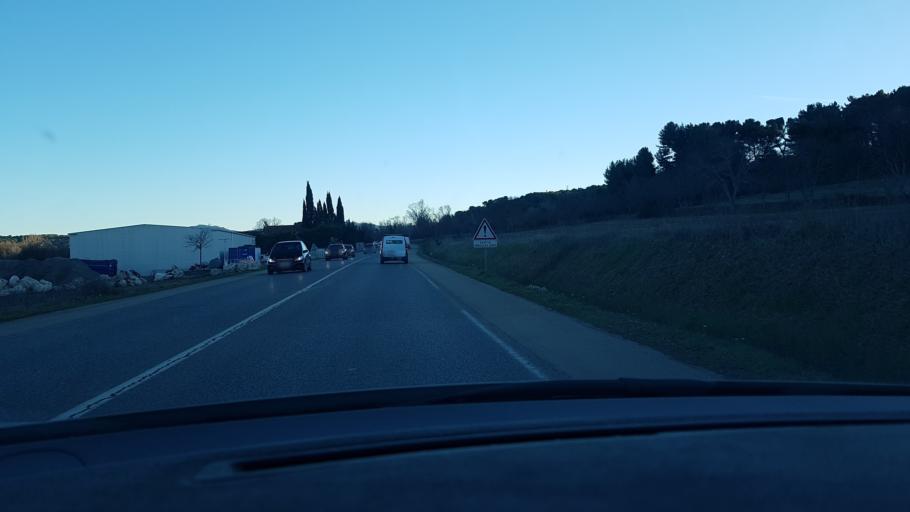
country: FR
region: Provence-Alpes-Cote d'Azur
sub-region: Departement des Bouches-du-Rhone
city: Bouc-Bel-Air
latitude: 43.4975
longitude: 5.4030
